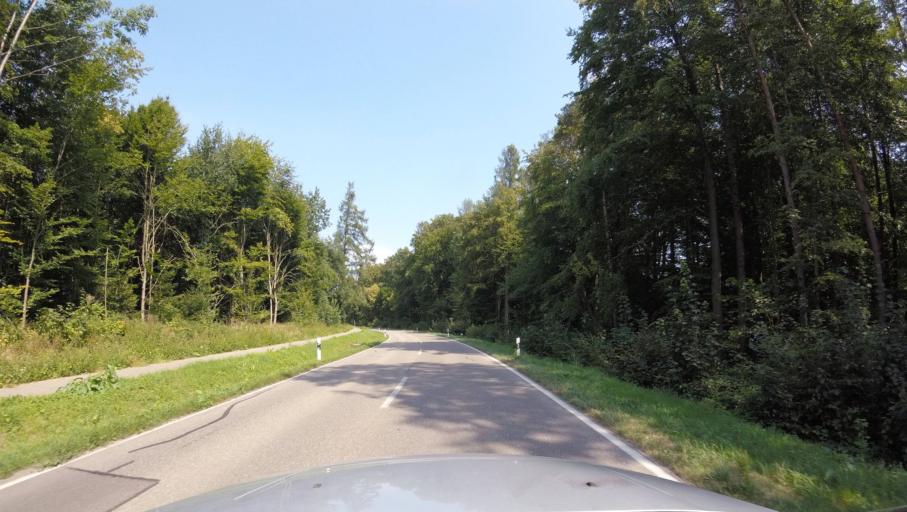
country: DE
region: Baden-Wuerttemberg
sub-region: Regierungsbezirk Stuttgart
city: Backnang
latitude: 48.9536
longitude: 9.4577
